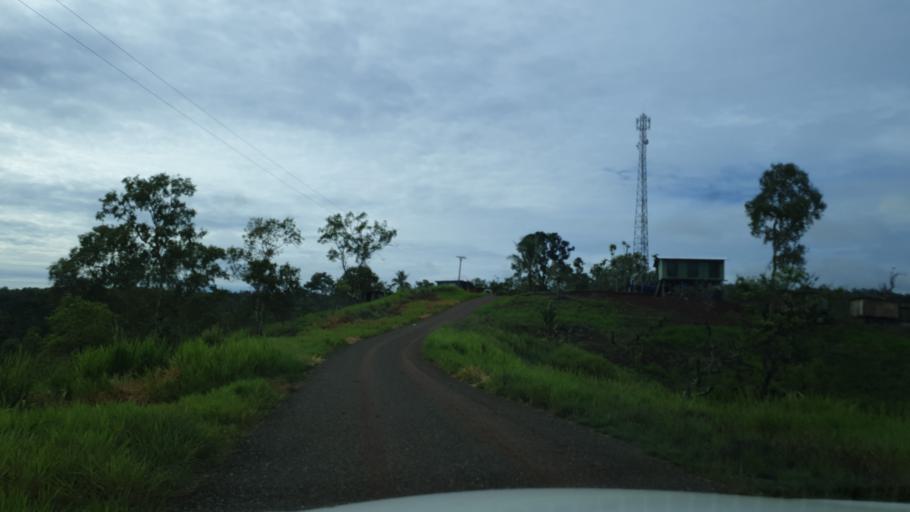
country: PG
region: National Capital
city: Port Moresby
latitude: -9.4286
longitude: 147.3940
